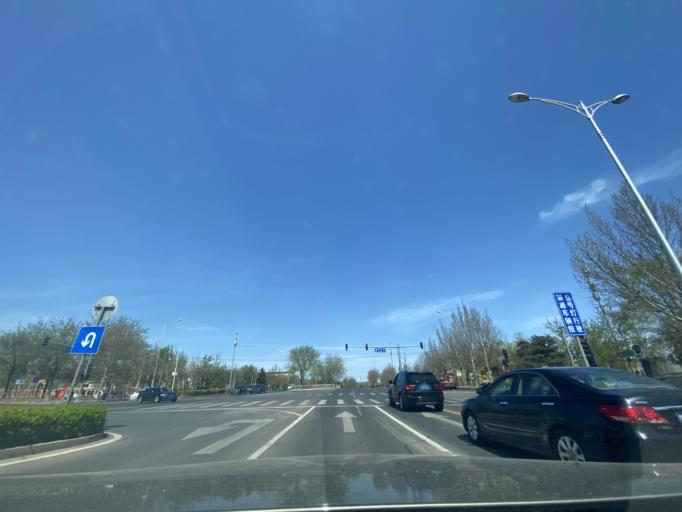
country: CN
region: Beijing
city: Sijiqing
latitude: 39.9388
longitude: 116.2404
